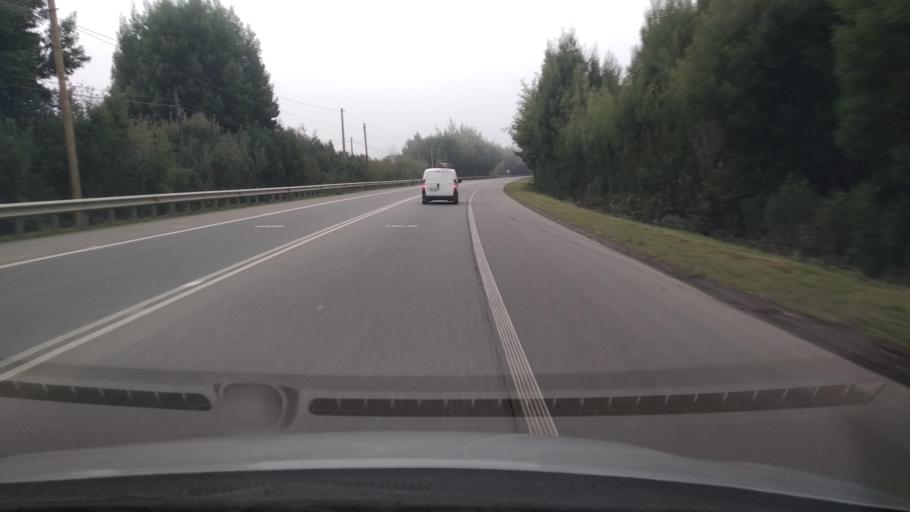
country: CL
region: Los Lagos
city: Las Animas
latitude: -39.7502
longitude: -73.2290
